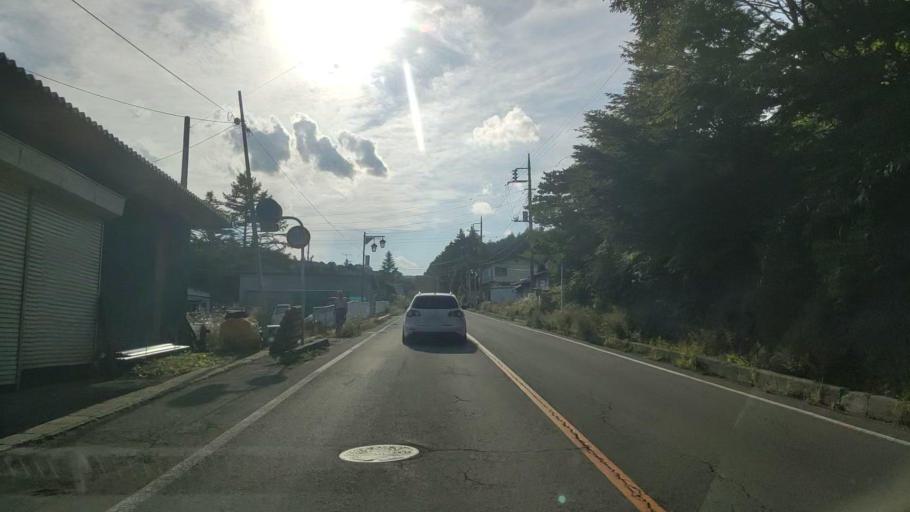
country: JP
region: Nagano
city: Komoro
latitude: 36.4862
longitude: 138.4319
